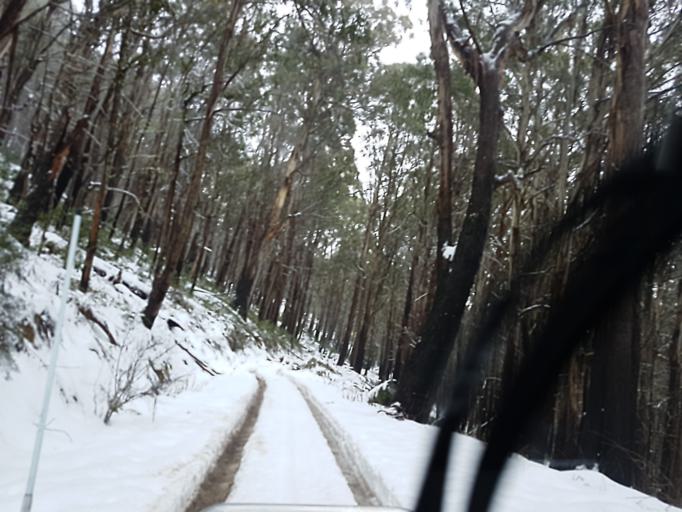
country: AU
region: Victoria
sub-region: Murrindindi
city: Alexandra
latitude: -37.4801
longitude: 145.9009
